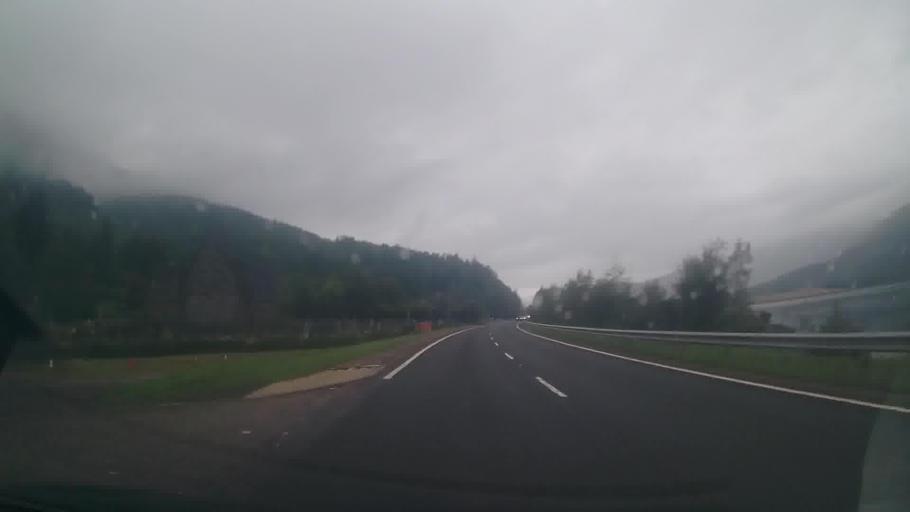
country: GB
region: Scotland
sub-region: Highland
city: Fort William
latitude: 56.6785
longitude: -5.1542
